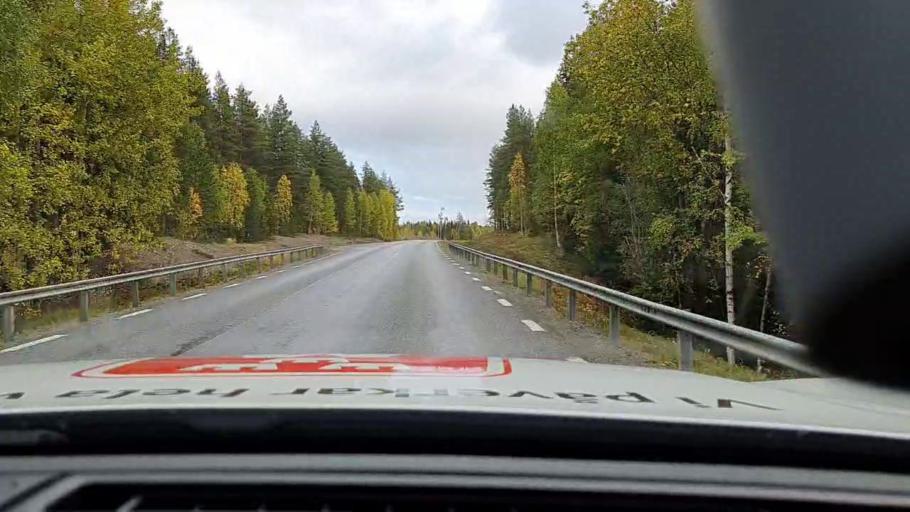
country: SE
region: Vaesterbotten
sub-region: Norsjo Kommun
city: Norsjoe
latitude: 64.9519
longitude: 19.6717
